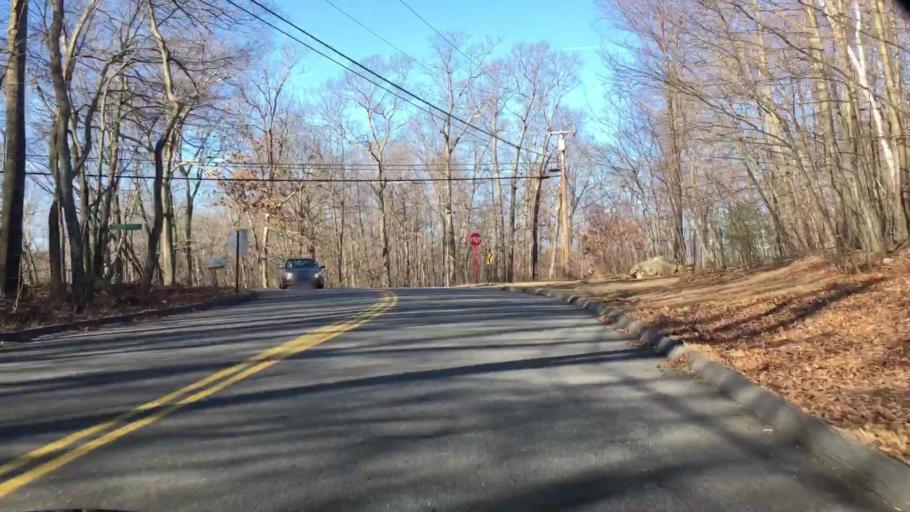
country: US
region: Connecticut
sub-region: Tolland County
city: Tolland
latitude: 41.8842
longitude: -72.3866
